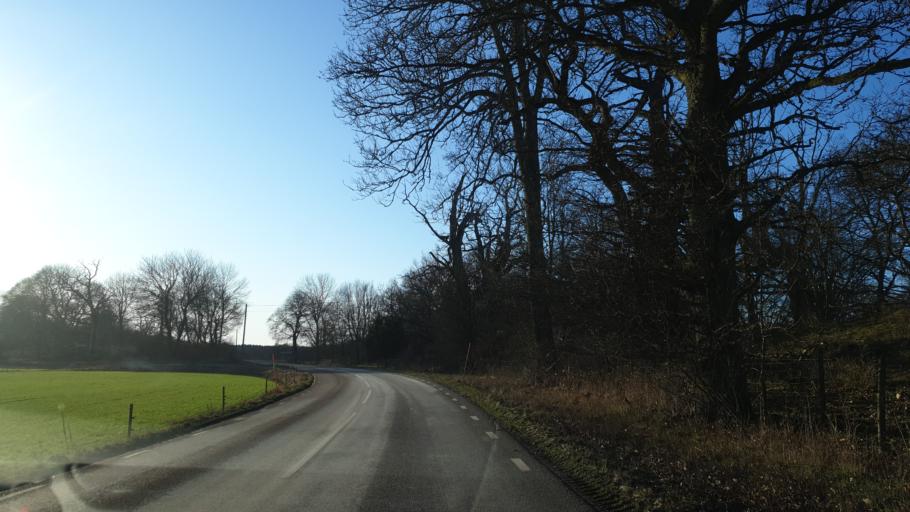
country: SE
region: Blekinge
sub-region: Karlskrona Kommun
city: Nattraby
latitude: 56.2422
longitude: 15.4204
